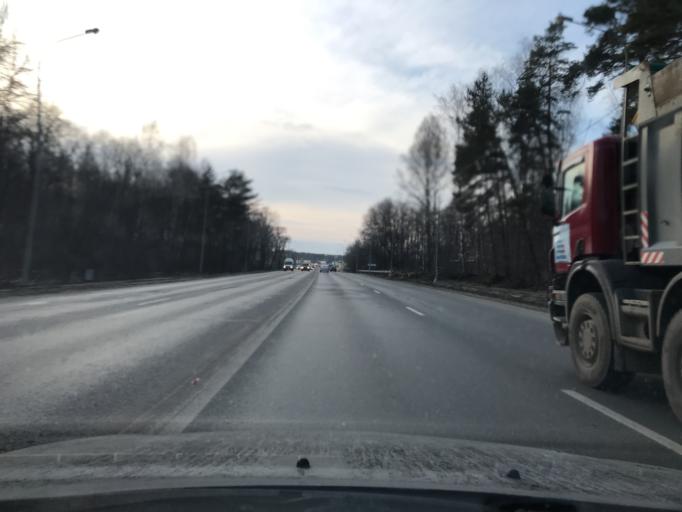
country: RU
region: Kaluga
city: Mstikhino
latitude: 54.5554
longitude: 36.1312
